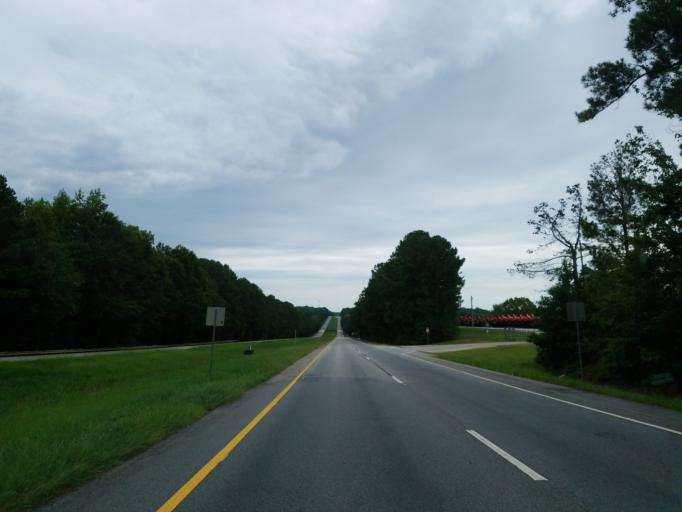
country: US
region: Georgia
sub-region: Spalding County
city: East Griffin
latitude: 33.1407
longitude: -84.2383
